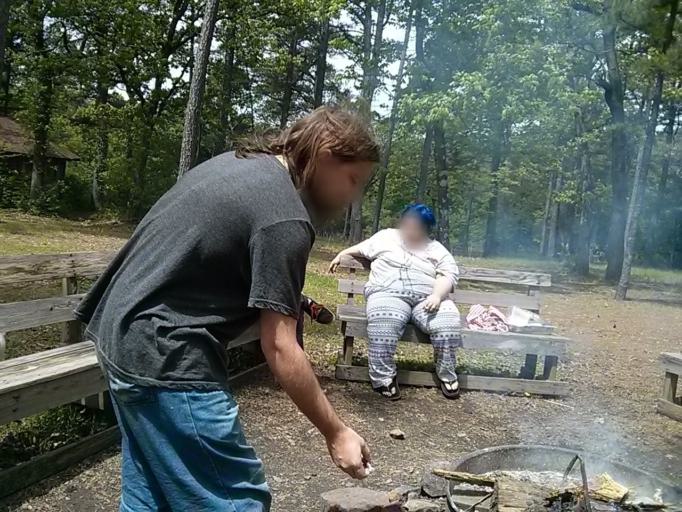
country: US
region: Oklahoma
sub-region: Latimer County
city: Wilburton
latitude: 35.0039
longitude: -95.3367
